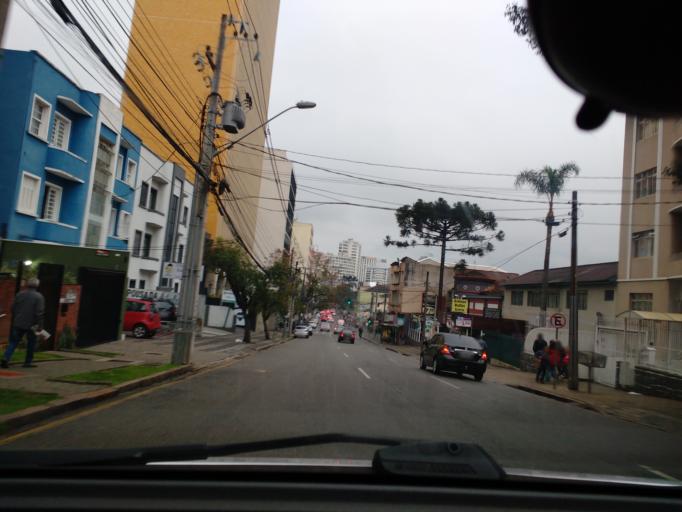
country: BR
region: Parana
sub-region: Curitiba
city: Curitiba
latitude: -25.4252
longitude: -49.2610
